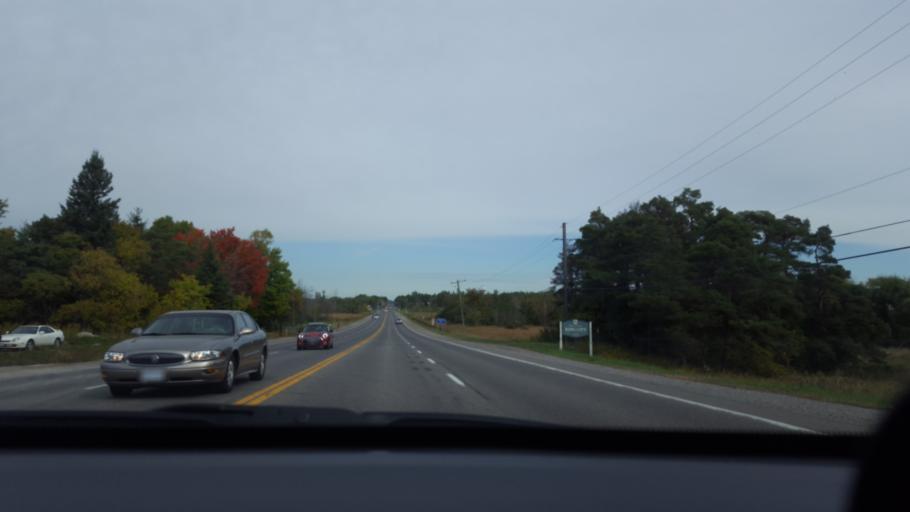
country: CA
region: Ontario
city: Vaughan
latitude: 43.9131
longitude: -79.5239
